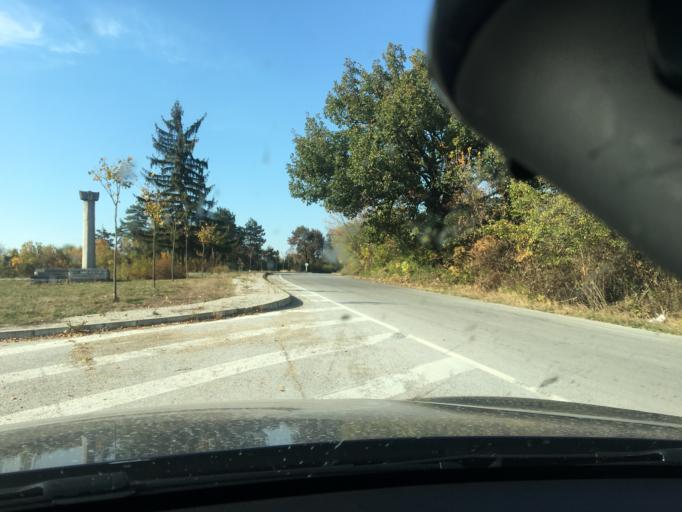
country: BG
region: Lovech
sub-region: Obshtina Yablanitsa
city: Yablanitsa
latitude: 43.0600
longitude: 24.2173
